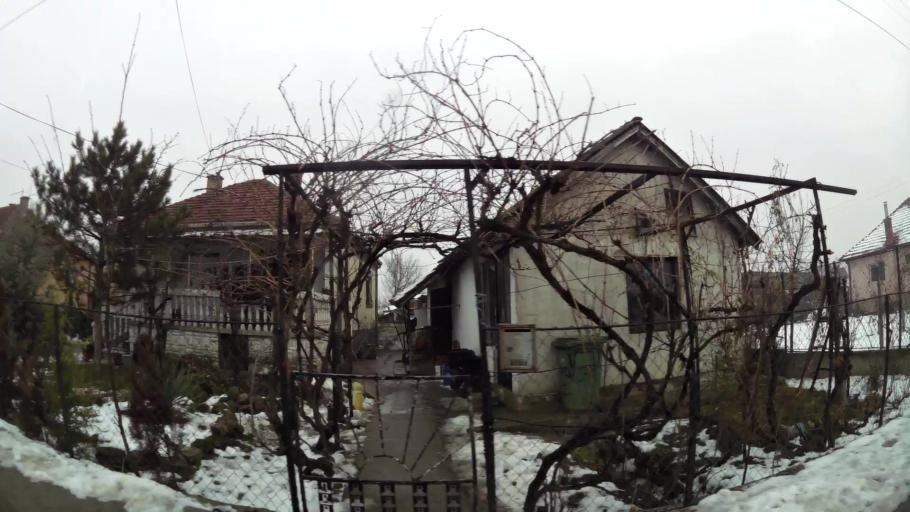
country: MK
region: Petrovec
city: Petrovec
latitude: 41.9419
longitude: 21.6119
